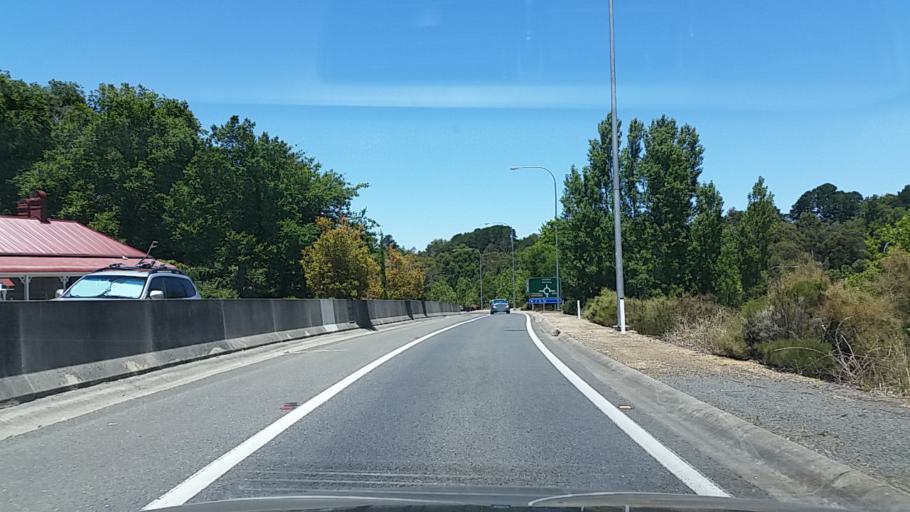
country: AU
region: South Australia
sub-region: Adelaide Hills
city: Crafers
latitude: -34.9957
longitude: 138.7010
